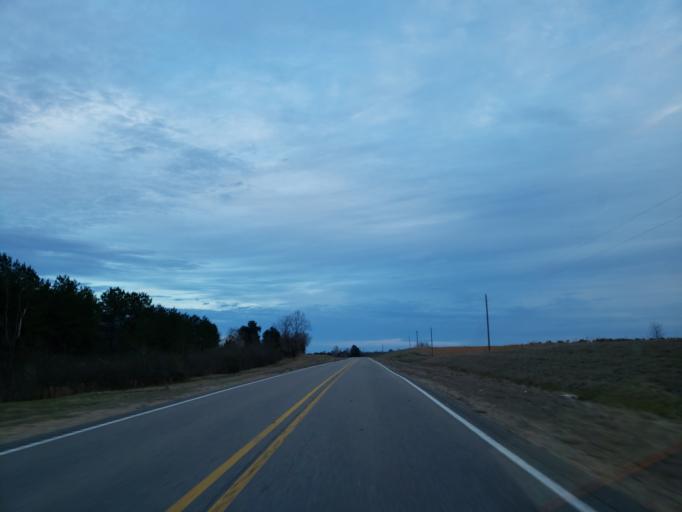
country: US
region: Mississippi
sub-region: Kemper County
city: De Kalb
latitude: 32.8309
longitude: -88.3878
